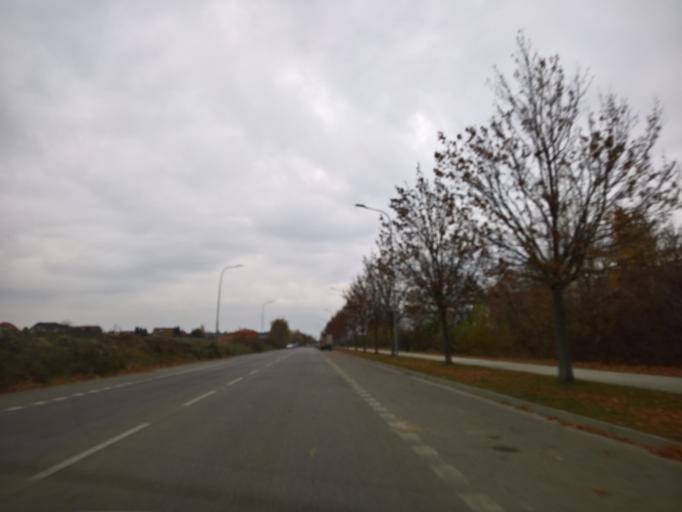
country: SK
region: Nitriansky
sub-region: Okres Nitra
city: Nitra
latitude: 48.2944
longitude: 18.0584
